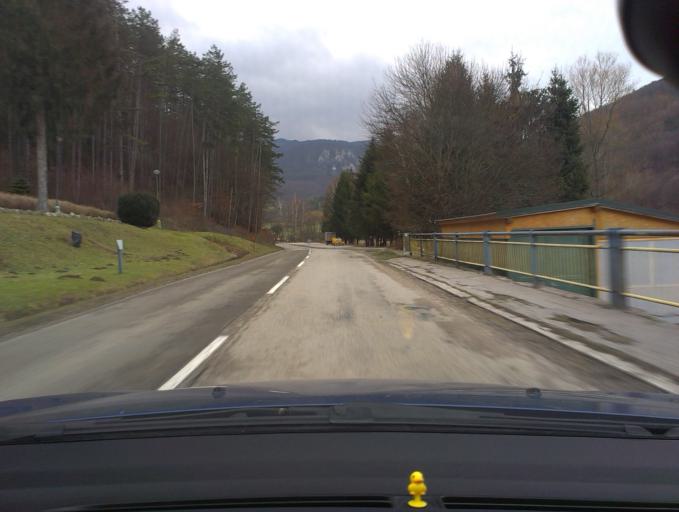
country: SK
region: Nitriansky
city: Trencianske Teplice
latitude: 48.8988
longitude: 18.2018
